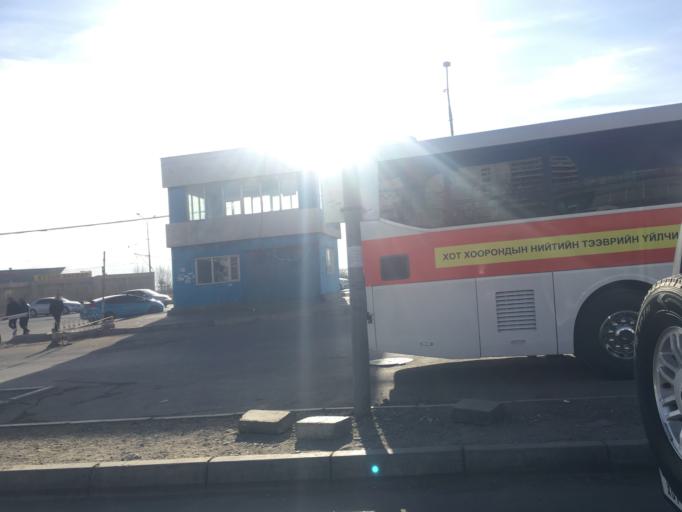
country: MN
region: Ulaanbaatar
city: Ulaanbaatar
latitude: 47.9109
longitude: 106.8227
